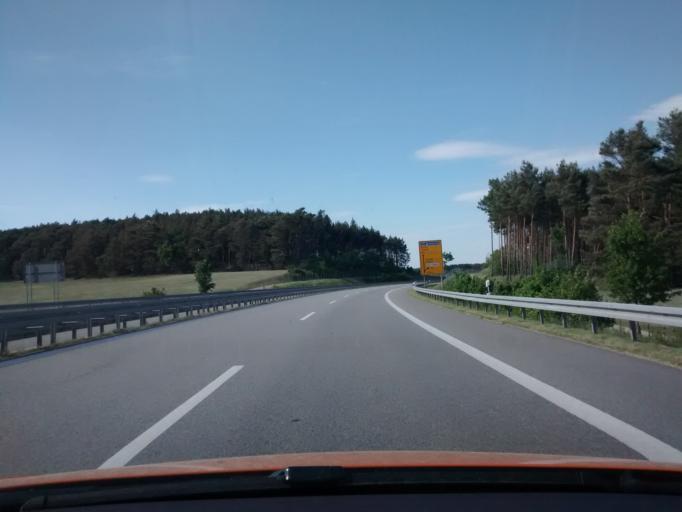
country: DE
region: Brandenburg
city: Trebbin
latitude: 52.2041
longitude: 13.2563
